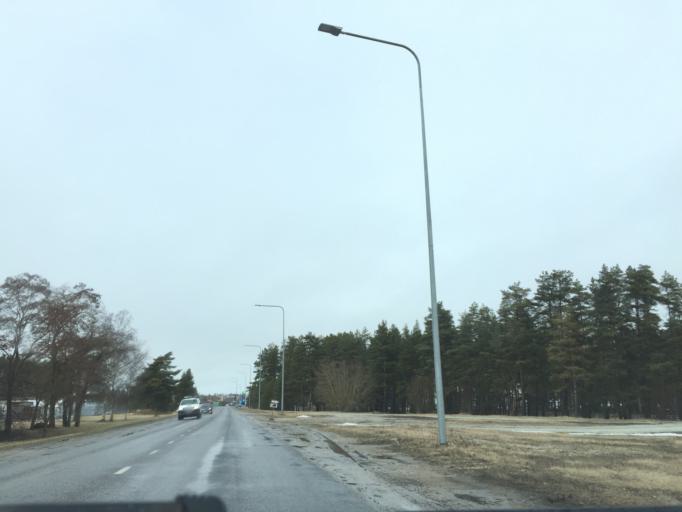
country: EE
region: Laeaene
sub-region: Haapsalu linn
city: Haapsalu
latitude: 58.9229
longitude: 23.5475
